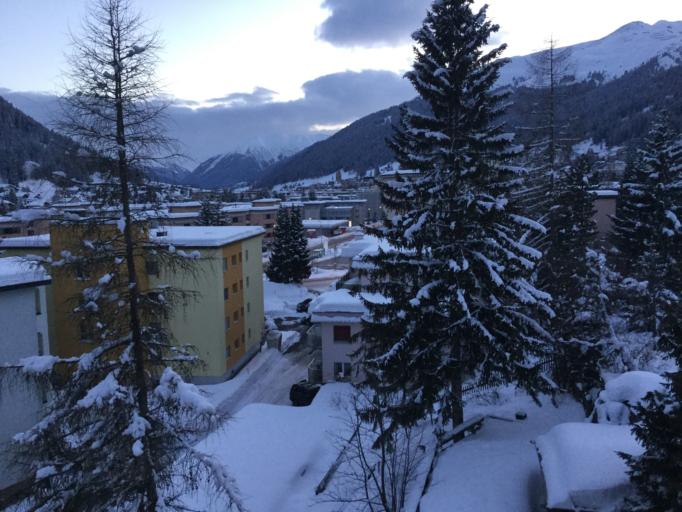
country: CH
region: Grisons
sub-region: Praettigau/Davos District
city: Davos
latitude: 46.8009
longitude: 9.8340
